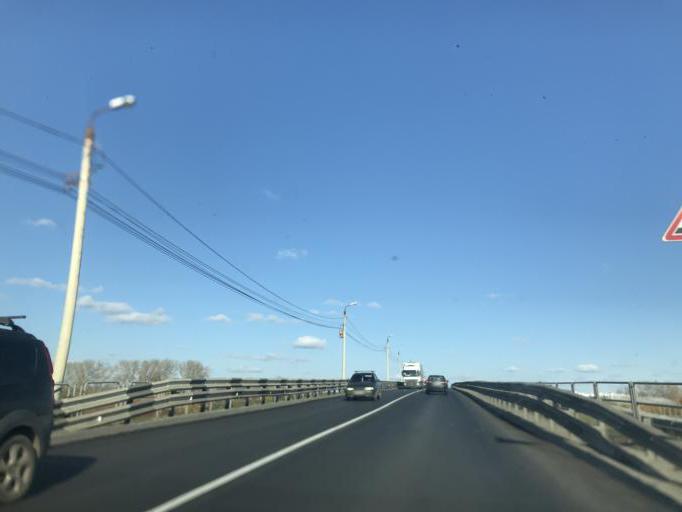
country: RU
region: Chelyabinsk
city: Roshchino
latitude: 55.2312
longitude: 61.2887
